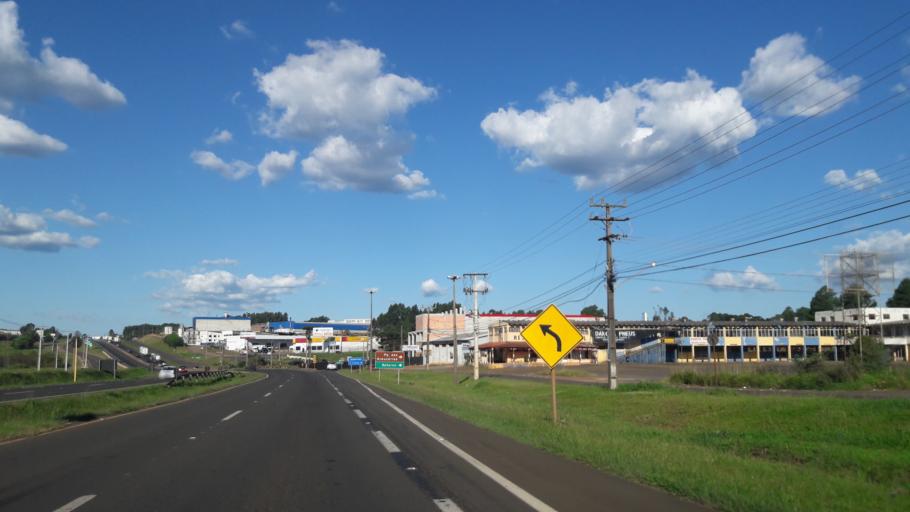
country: BR
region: Parana
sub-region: Guarapuava
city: Guarapuava
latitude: -25.3584
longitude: -51.4647
